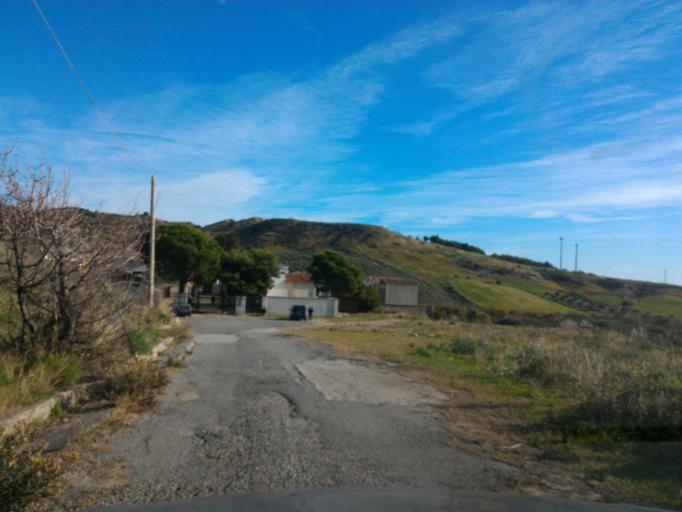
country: IT
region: Calabria
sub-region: Provincia di Catanzaro
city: Cropani Marina
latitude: 38.9293
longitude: 16.8065
